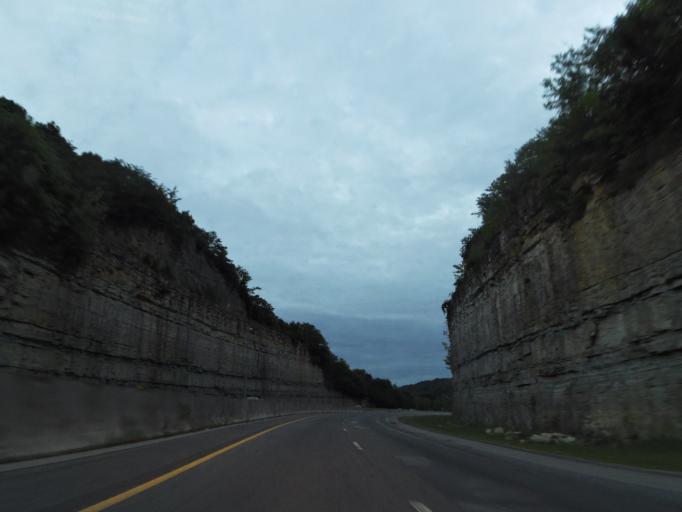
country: US
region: Tennessee
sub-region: Davidson County
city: Nashville
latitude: 36.2275
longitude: -86.8596
